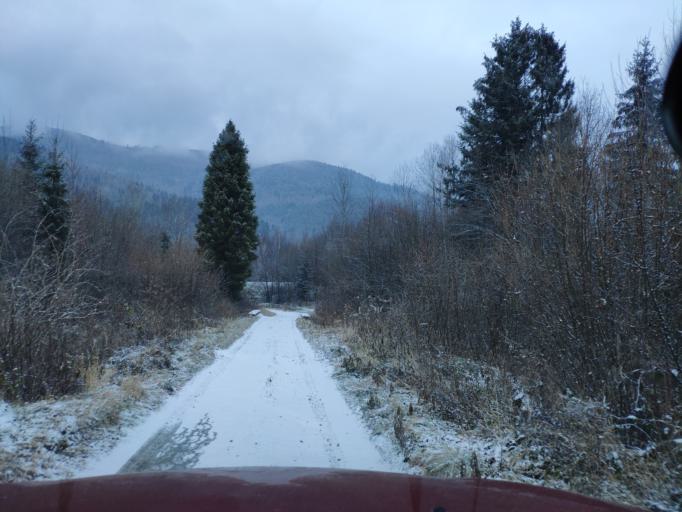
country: SK
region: Kosicky
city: Spisska Nova Ves
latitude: 48.8129
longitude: 20.5713
